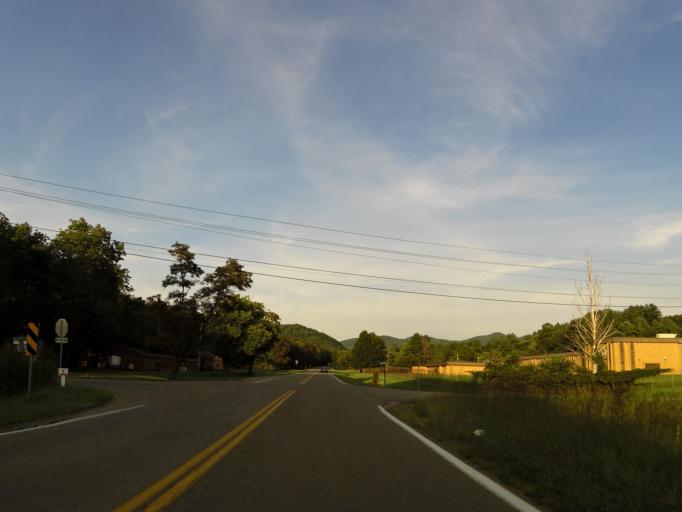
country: US
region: Virginia
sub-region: Washington County
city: Emory
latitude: 36.6409
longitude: -81.8131
